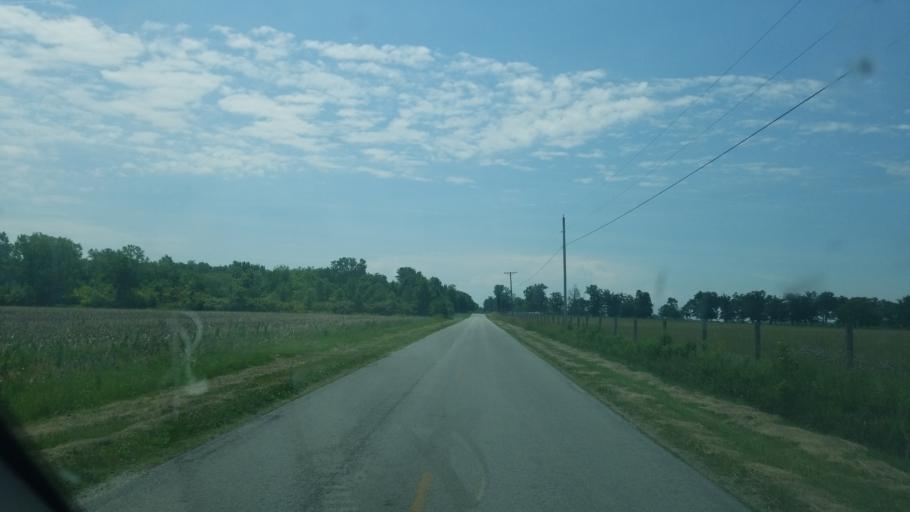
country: US
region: Ohio
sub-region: Wood County
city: North Baltimore
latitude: 41.2373
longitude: -83.6212
